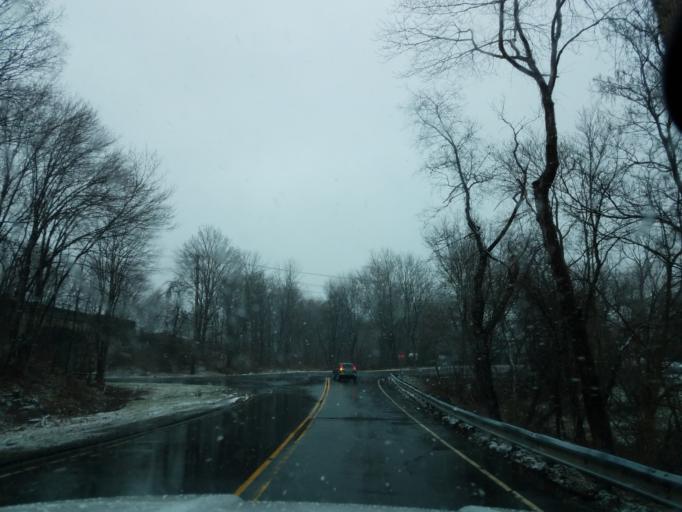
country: US
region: Connecticut
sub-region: New Haven County
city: Meriden
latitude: 41.5117
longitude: -72.7817
